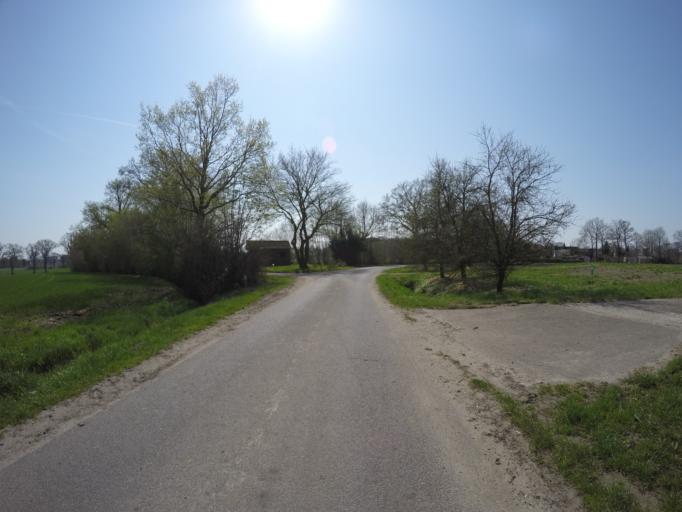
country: DE
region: Schleswig-Holstein
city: Bilsen
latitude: 53.7574
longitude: 9.8597
